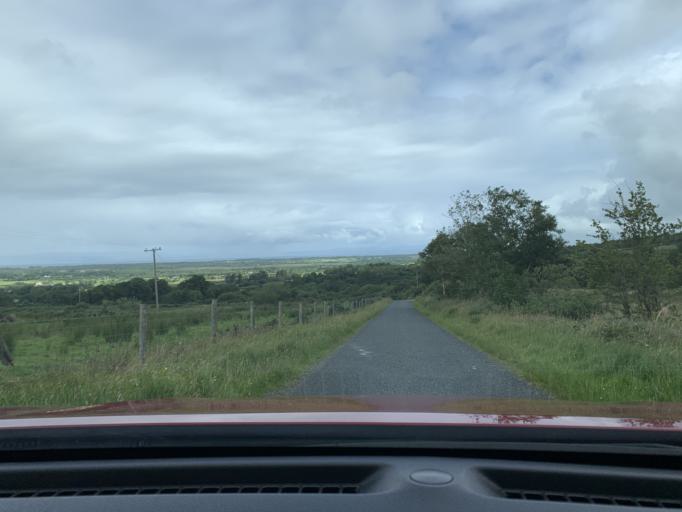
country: IE
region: Connaught
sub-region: County Leitrim
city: Kinlough
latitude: 54.3960
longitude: -8.4024
